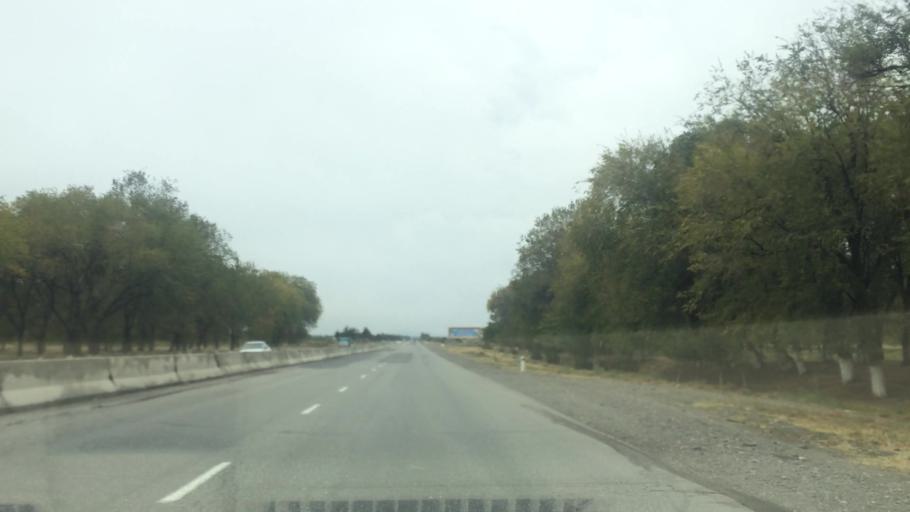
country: UZ
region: Samarqand
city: Bulung'ur
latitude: 39.7944
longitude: 67.3286
